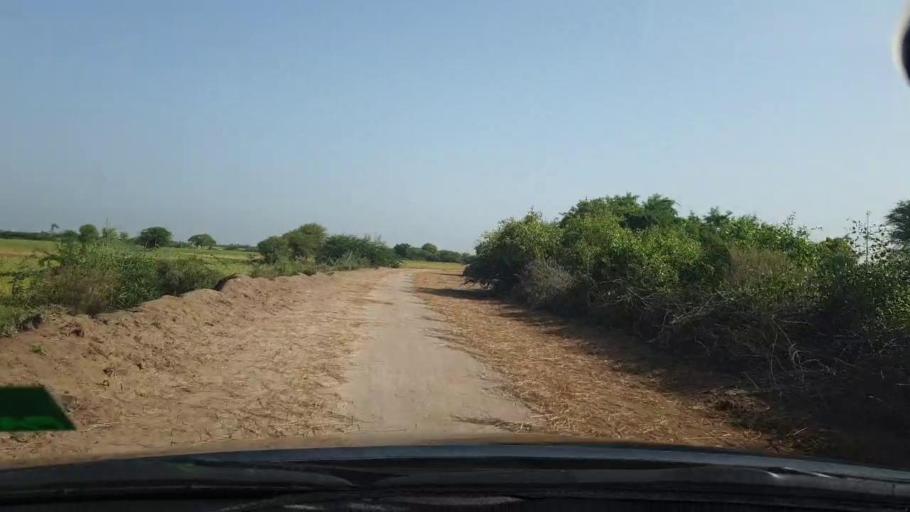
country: PK
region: Sindh
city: Tando Bago
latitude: 24.7225
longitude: 68.9965
